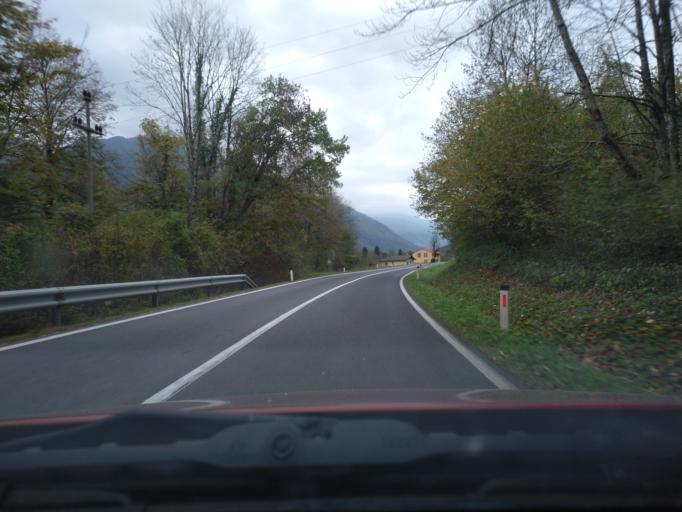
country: IT
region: Friuli Venezia Giulia
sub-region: Provincia di Udine
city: Cras
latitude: 46.2105
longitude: 13.6311
